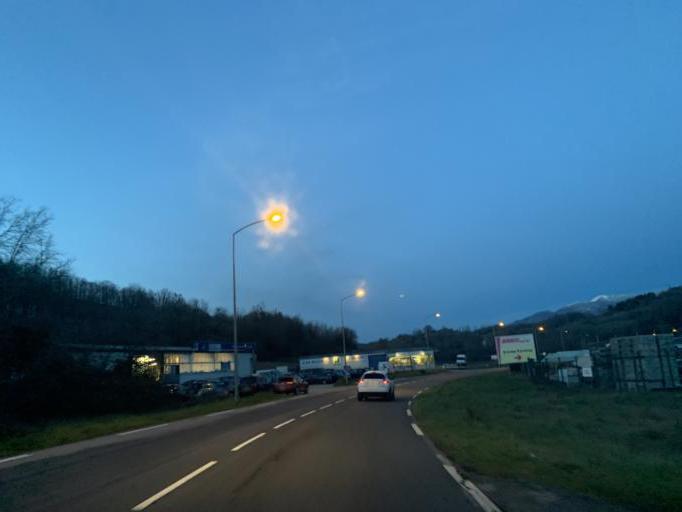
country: FR
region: Rhone-Alpes
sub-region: Departement de l'Ain
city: Belley
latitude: 45.7763
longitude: 5.6872
